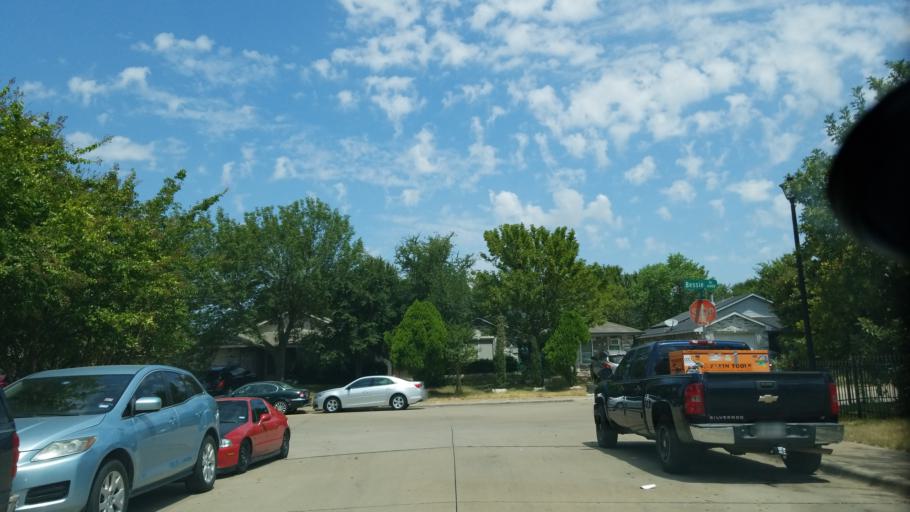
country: US
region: Texas
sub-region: Dallas County
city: Cockrell Hill
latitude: 32.7286
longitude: -96.8950
